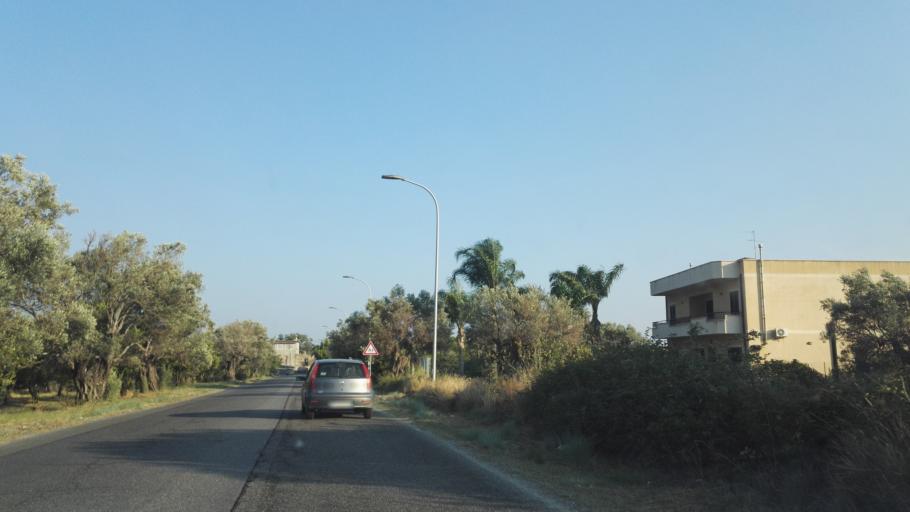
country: IT
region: Calabria
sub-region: Provincia di Reggio Calabria
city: Marina di Gioiosa Ionica
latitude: 38.3109
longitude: 16.3151
